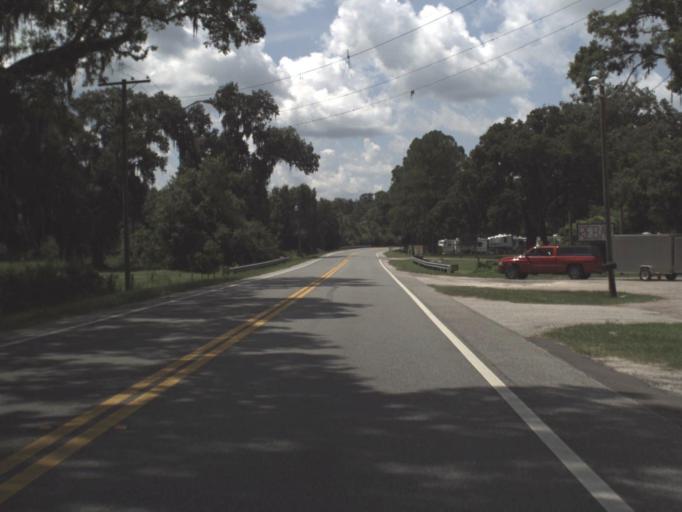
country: US
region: Florida
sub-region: Hernando County
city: Brooksville
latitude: 28.5741
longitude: -82.3751
